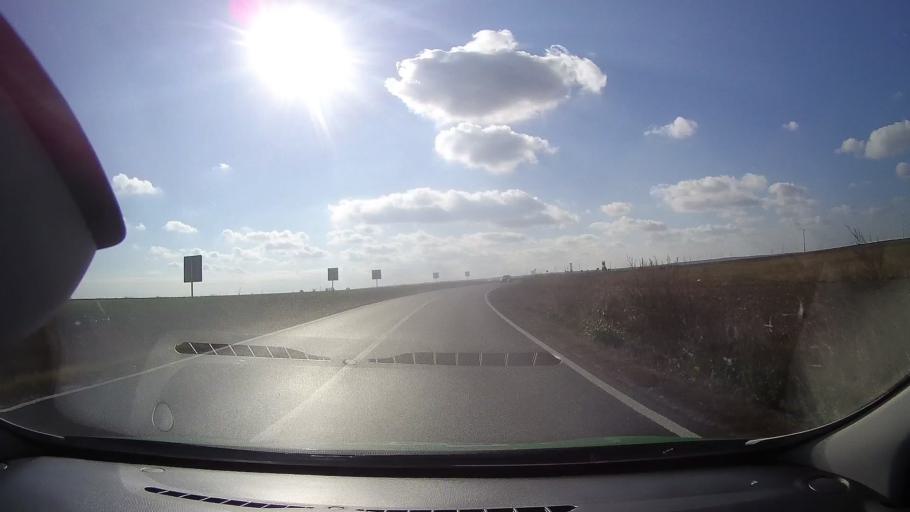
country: RO
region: Constanta
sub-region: Comuna Mihai Viteazu
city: Mihai Viteazu
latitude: 44.6678
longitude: 28.6828
